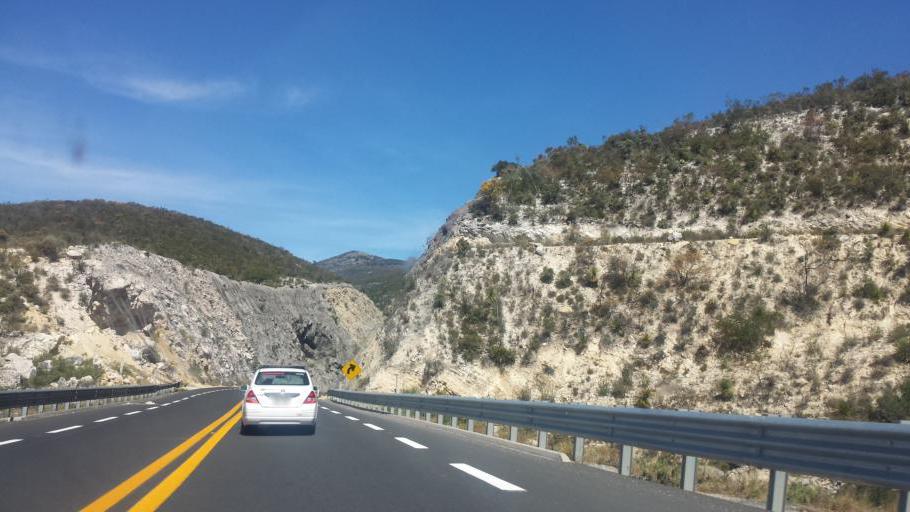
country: MX
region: Puebla
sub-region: San Jose Miahuatlan
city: San Pedro Tetitlan
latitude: 18.0177
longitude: -97.3526
